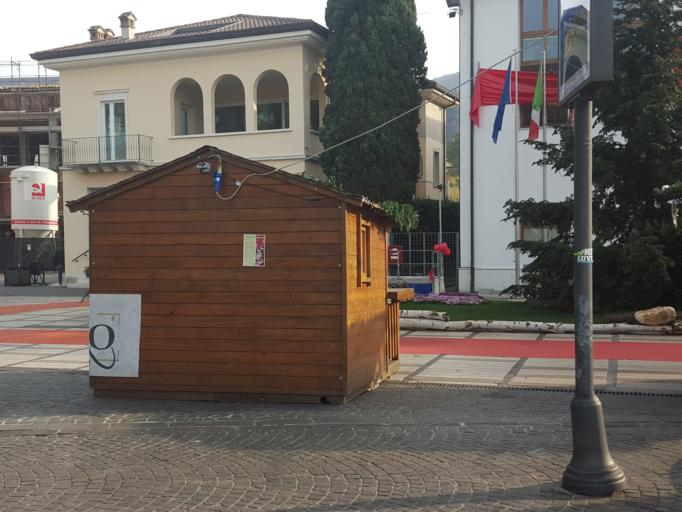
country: IT
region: Veneto
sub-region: Provincia di Verona
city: Garda
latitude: 45.5744
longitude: 10.7072
